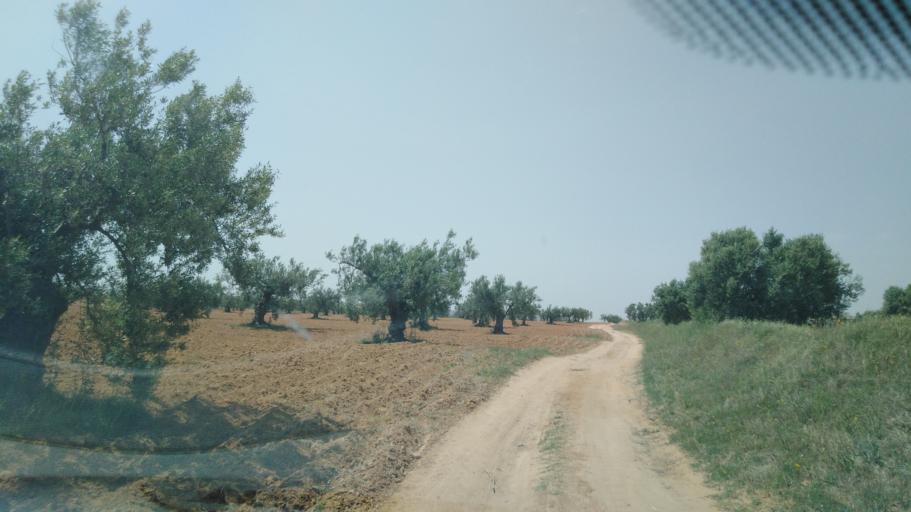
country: TN
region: Safaqis
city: Sfax
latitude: 34.7624
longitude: 10.5774
